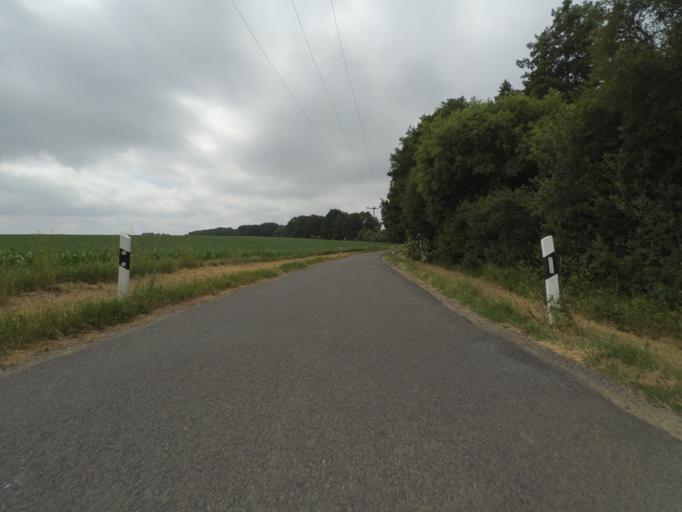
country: DE
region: Mecklenburg-Vorpommern
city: Krakow am See
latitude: 53.6569
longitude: 12.3481
